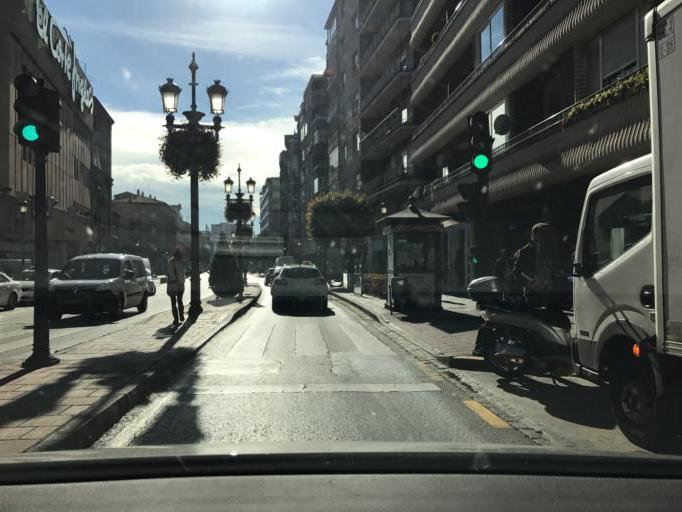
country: ES
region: Andalusia
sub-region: Provincia de Granada
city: Granada
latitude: 37.1707
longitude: -3.5983
